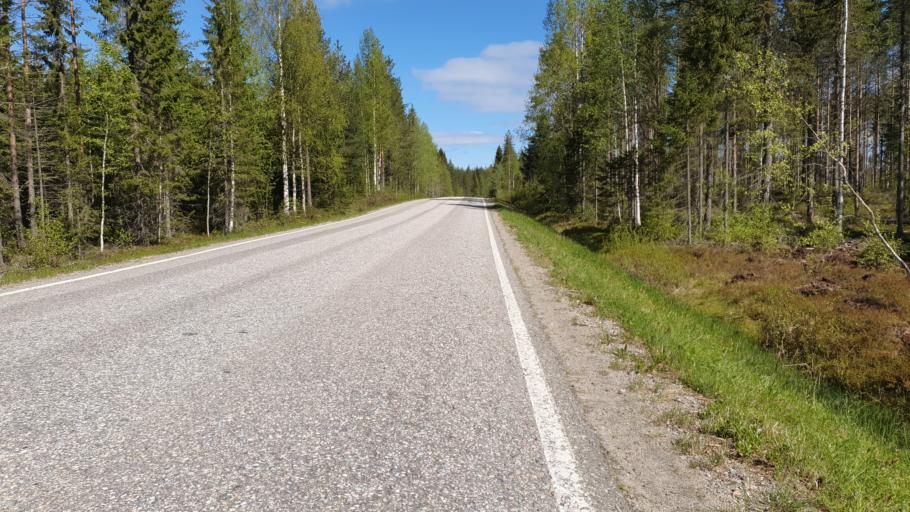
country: FI
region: Kainuu
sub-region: Kehys-Kainuu
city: Kuhmo
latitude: 64.1872
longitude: 29.4446
